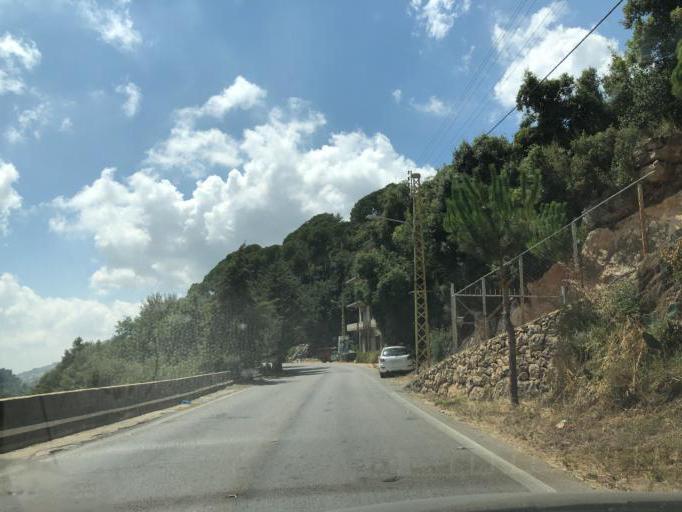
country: LB
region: Mont-Liban
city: Beit ed Dine
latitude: 33.7005
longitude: 35.5962
